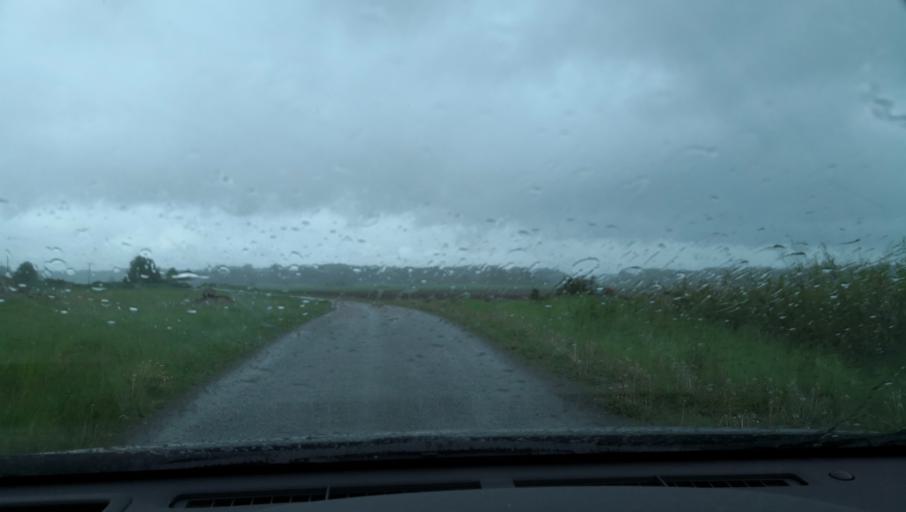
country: SE
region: Uppsala
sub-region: Enkopings Kommun
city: Orsundsbro
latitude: 59.7746
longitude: 17.3483
